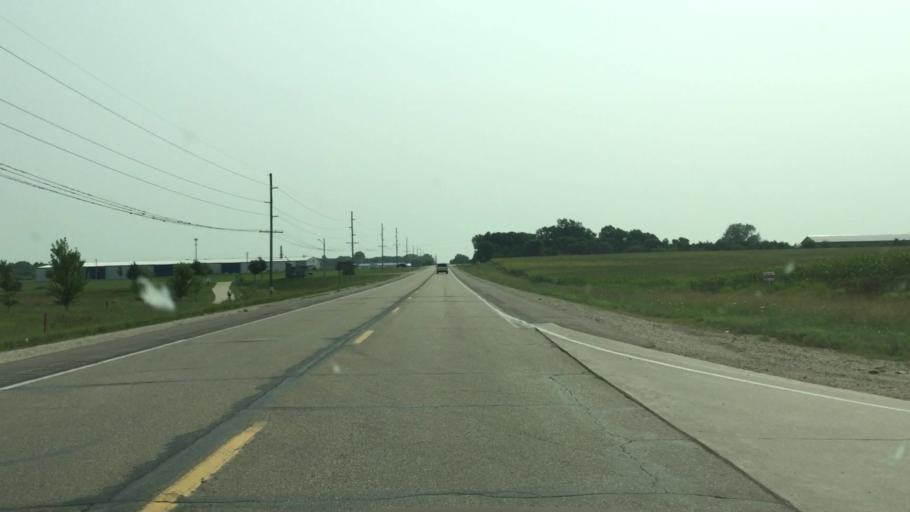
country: US
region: Iowa
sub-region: Dickinson County
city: Milford
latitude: 43.3424
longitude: -95.1646
